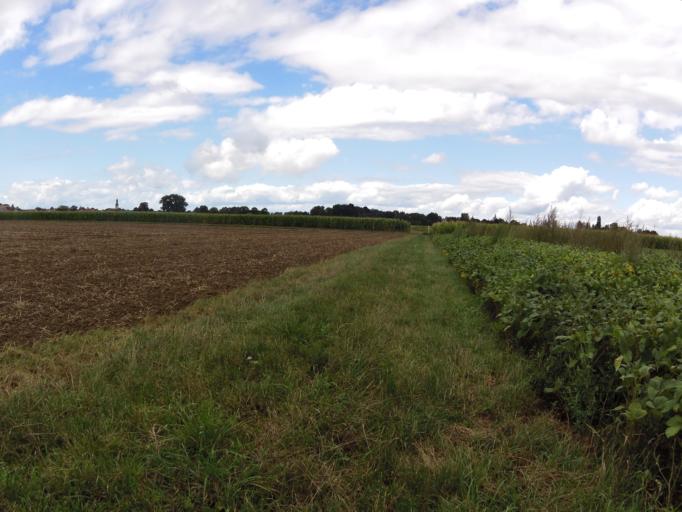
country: DE
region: Baden-Wuerttemberg
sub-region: Freiburg Region
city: Lahr
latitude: 48.3641
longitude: 7.8496
